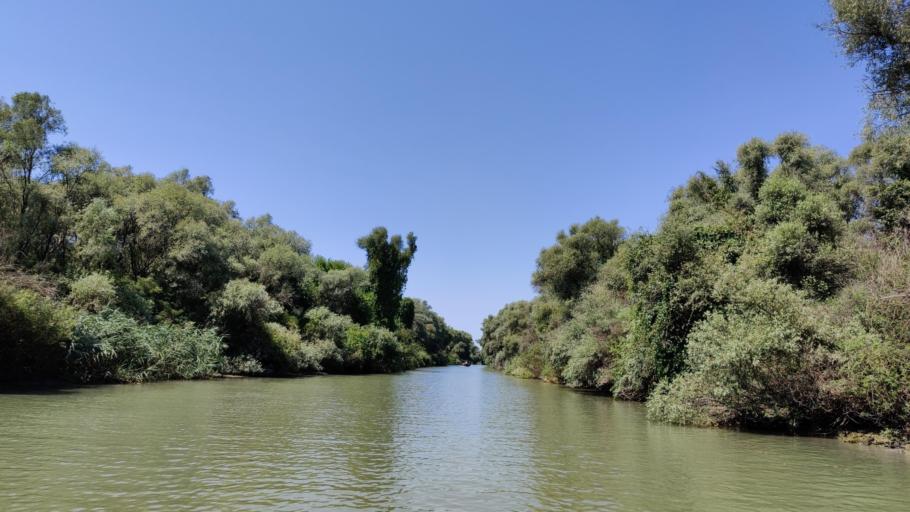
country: RO
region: Tulcea
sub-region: Comuna Pardina
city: Pardina
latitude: 45.2537
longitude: 28.9483
